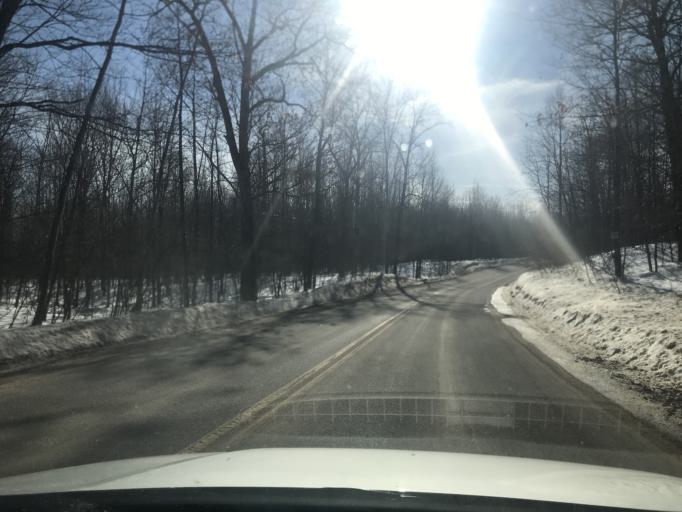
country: US
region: Michigan
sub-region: Dickinson County
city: Kingsford
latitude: 45.4006
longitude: -88.3413
